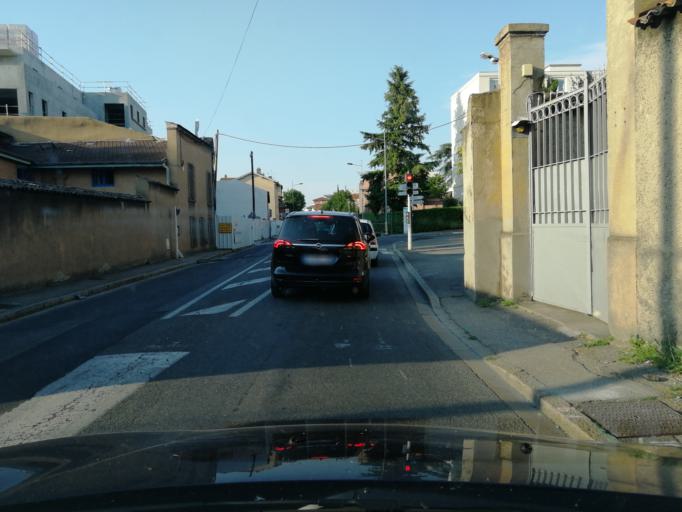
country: FR
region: Rhone-Alpes
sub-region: Departement du Rhone
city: Sathonay-Camp
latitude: 45.8074
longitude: 4.8558
